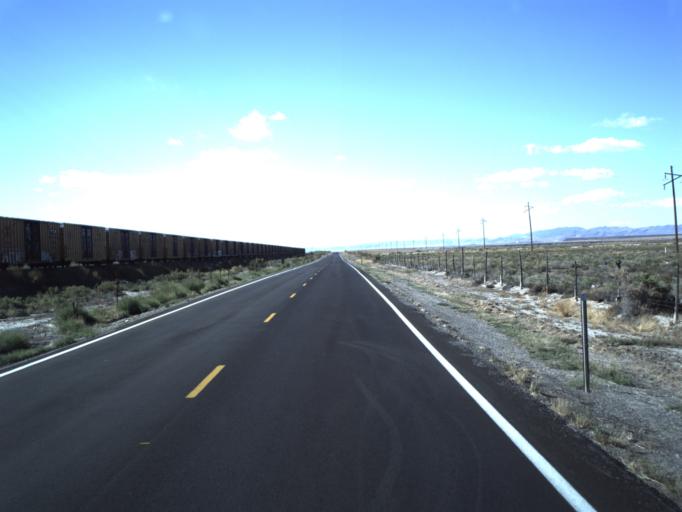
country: US
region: Utah
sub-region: Millard County
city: Delta
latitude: 39.2354
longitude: -112.6660
